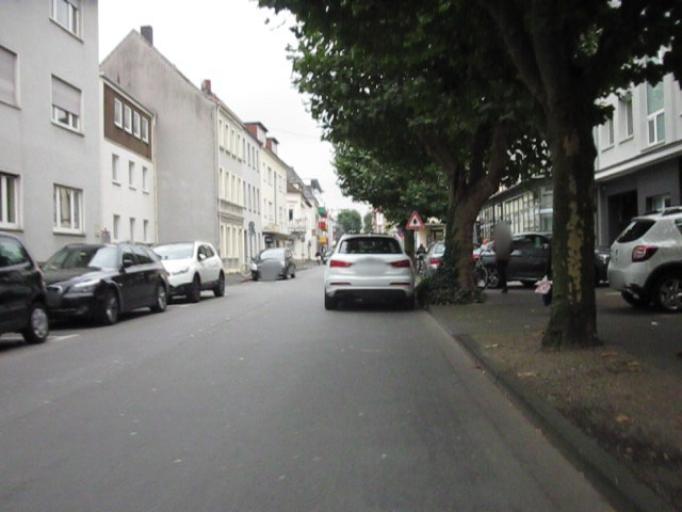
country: DE
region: North Rhine-Westphalia
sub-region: Regierungsbezirk Detmold
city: Paderborn
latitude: 51.7161
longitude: 8.7404
